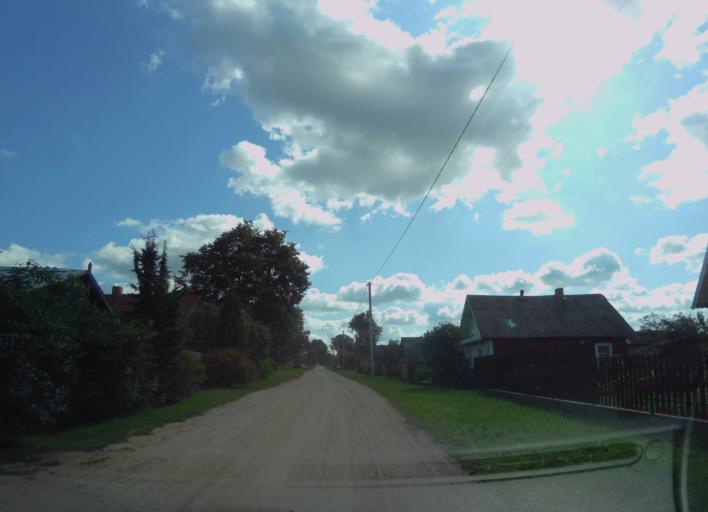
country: BY
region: Minsk
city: Zyembin
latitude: 54.3771
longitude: 28.3721
